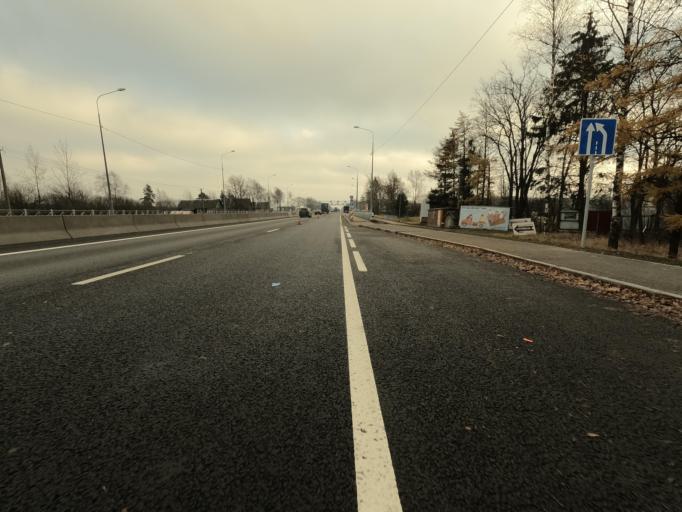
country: RU
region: Leningrad
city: Mga
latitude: 59.7251
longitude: 31.0949
